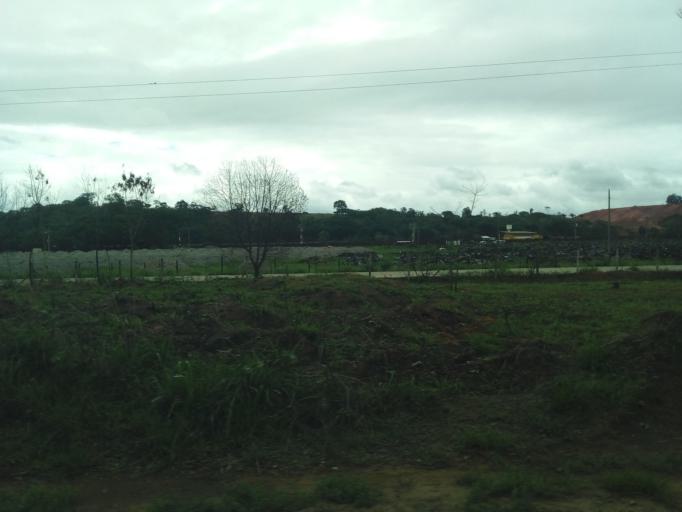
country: BR
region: Minas Gerais
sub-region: Ipatinga
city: Ipatinga
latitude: -19.4746
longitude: -42.4851
